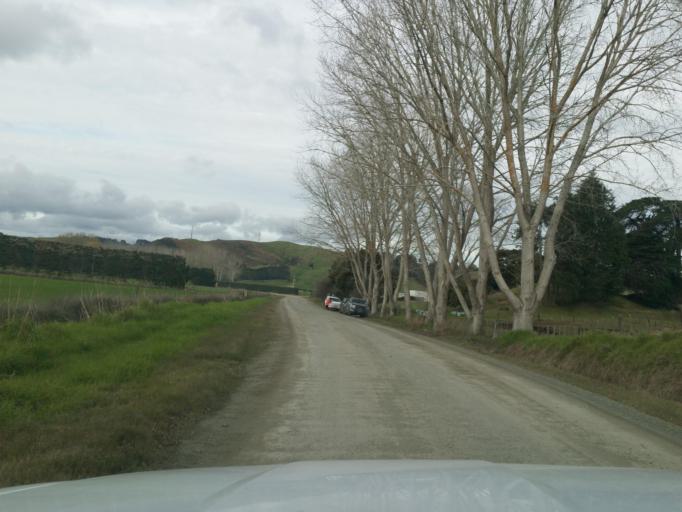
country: NZ
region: Northland
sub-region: Kaipara District
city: Dargaville
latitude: -35.8787
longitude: 173.9367
